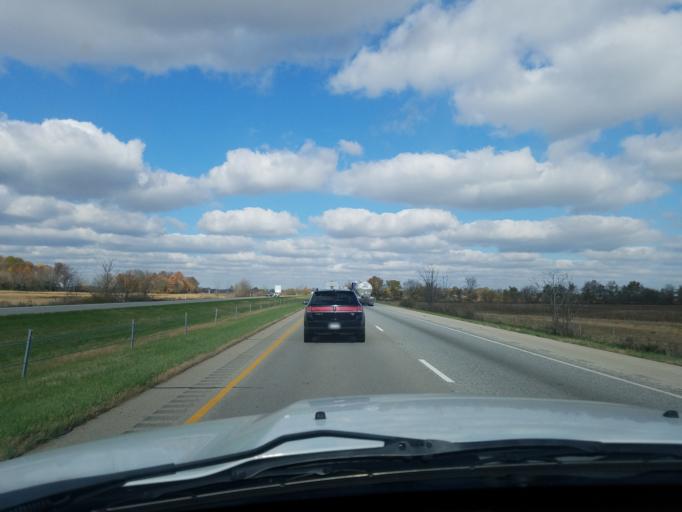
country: US
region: Indiana
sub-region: Bartholomew County
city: Lowell
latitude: 39.2320
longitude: -85.9541
